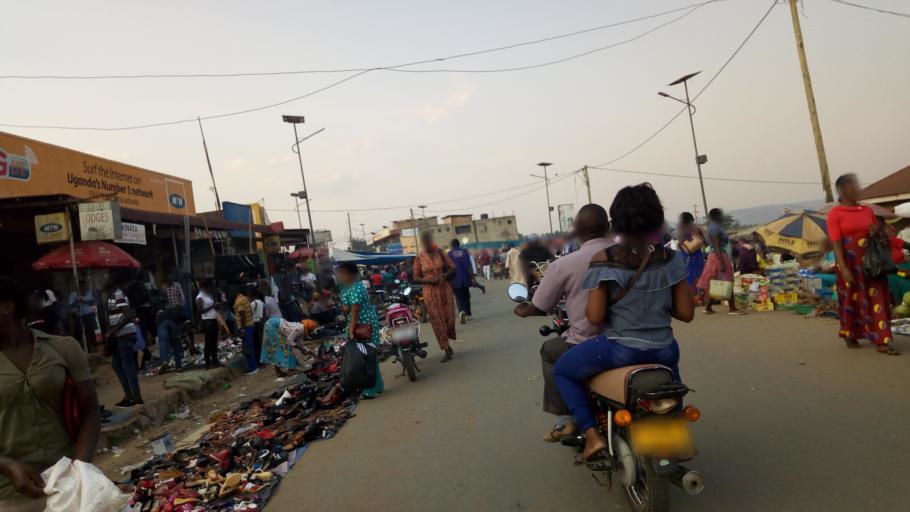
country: UG
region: Western Region
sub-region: Mbarara District
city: Mbarara
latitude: -0.5989
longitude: 30.6654
